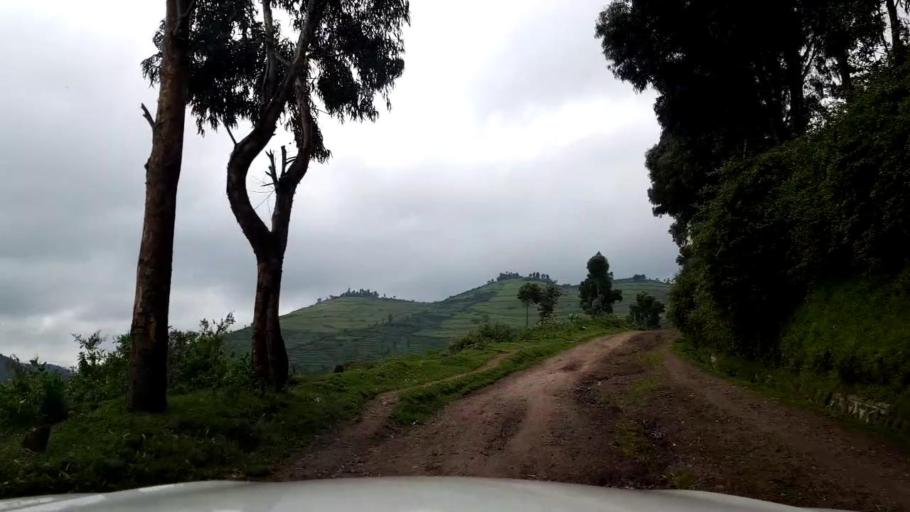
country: RW
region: Western Province
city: Gisenyi
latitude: -1.6640
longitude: 29.4183
